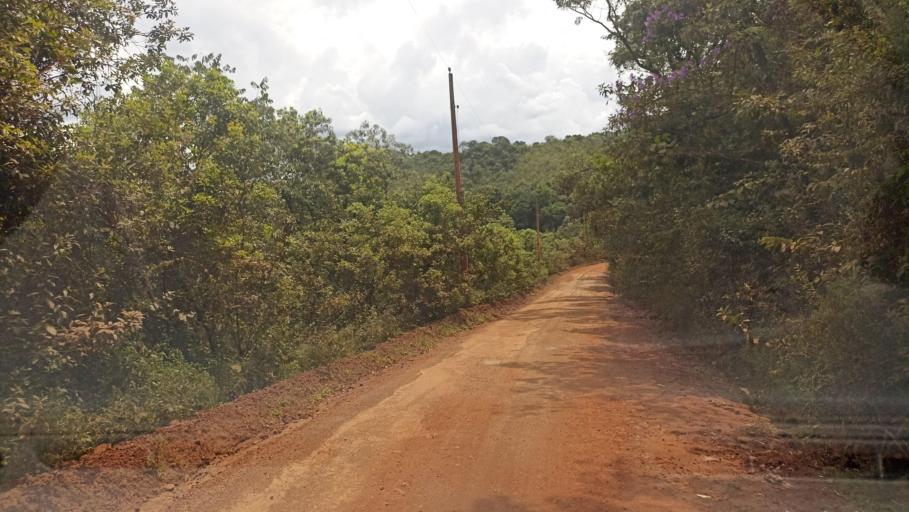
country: BR
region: Minas Gerais
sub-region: Itabirito
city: Itabirito
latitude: -20.3375
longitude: -43.7628
